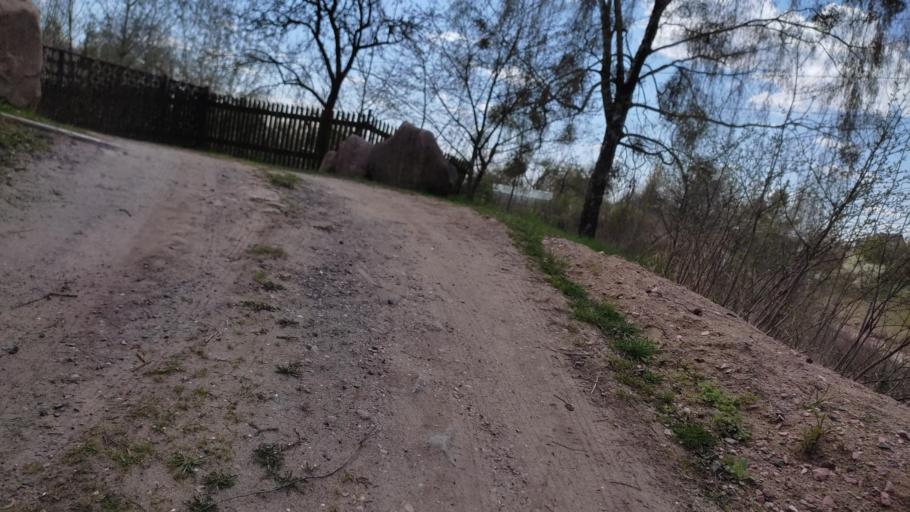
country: BY
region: Grodnenskaya
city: Hrodna
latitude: 53.6582
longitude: 23.8923
